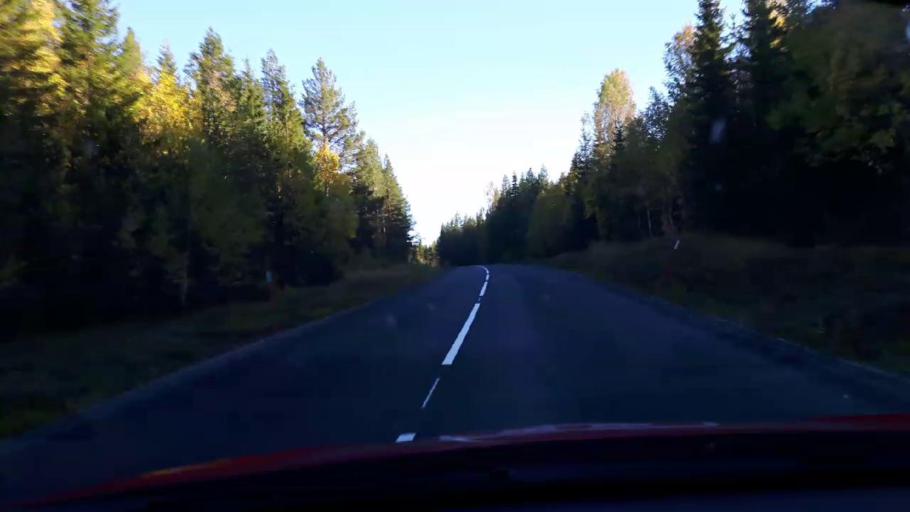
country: SE
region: Jaemtland
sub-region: OEstersunds Kommun
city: Lit
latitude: 63.4185
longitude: 14.8721
